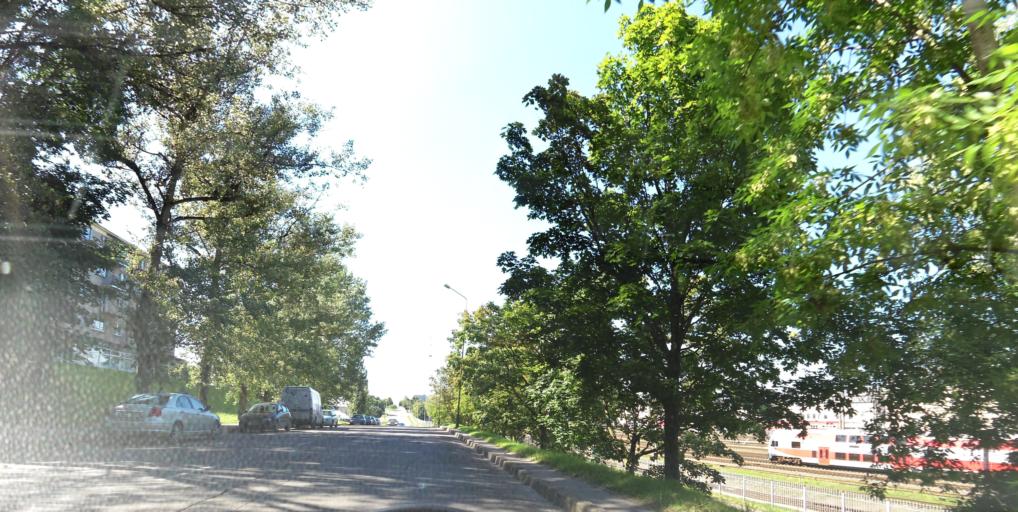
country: LT
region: Vilnius County
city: Naujamiestis
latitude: 54.6671
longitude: 25.2802
